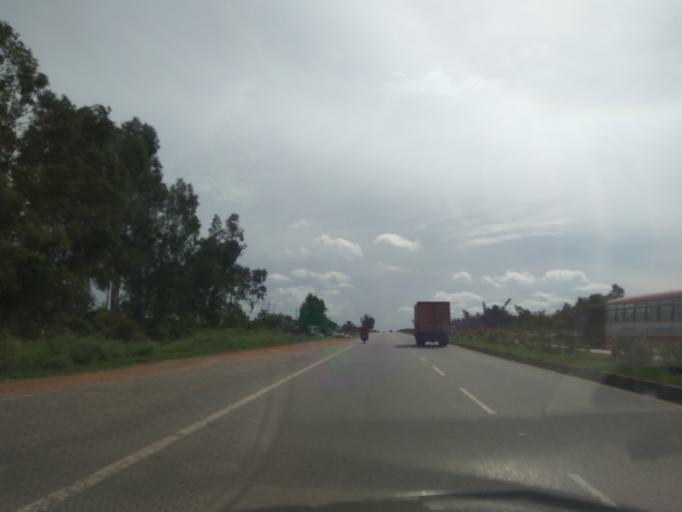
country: IN
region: Karnataka
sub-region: Bangalore Rural
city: Dasarahalli
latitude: 13.0949
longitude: 77.8467
